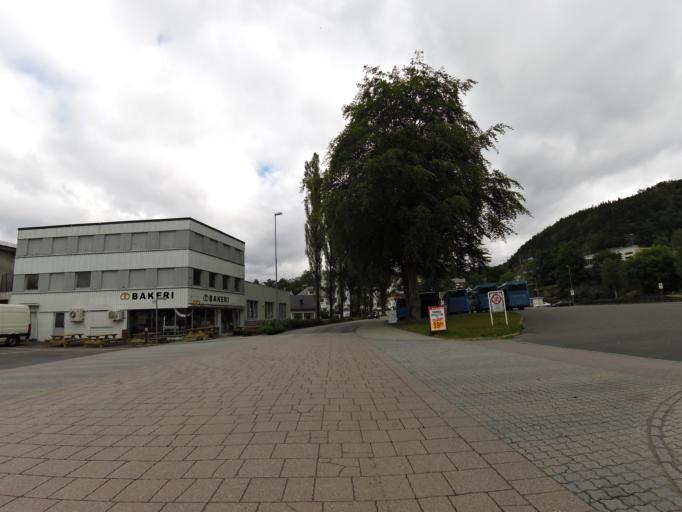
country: NO
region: Vest-Agder
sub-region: Flekkefjord
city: Flekkefjord
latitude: 58.2943
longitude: 6.6658
